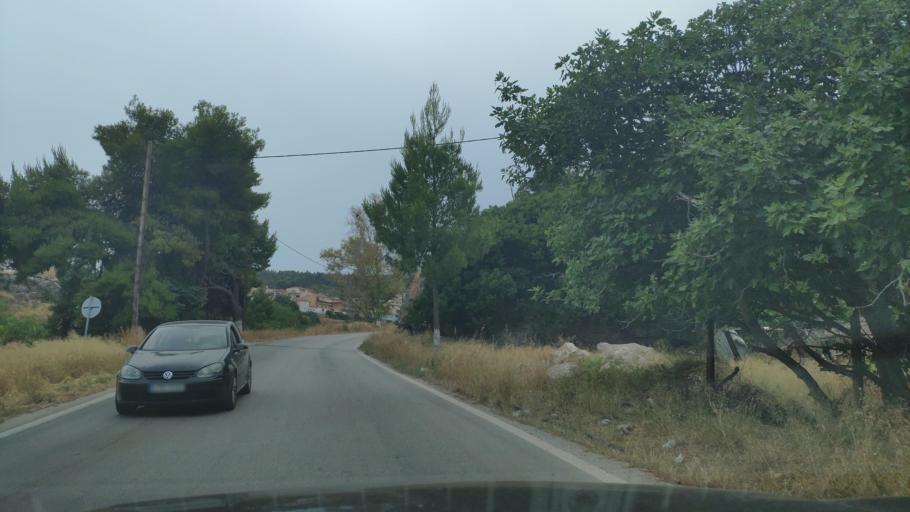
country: GR
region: Peloponnese
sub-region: Nomos Argolidos
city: Kranidi
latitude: 37.3840
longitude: 23.1548
